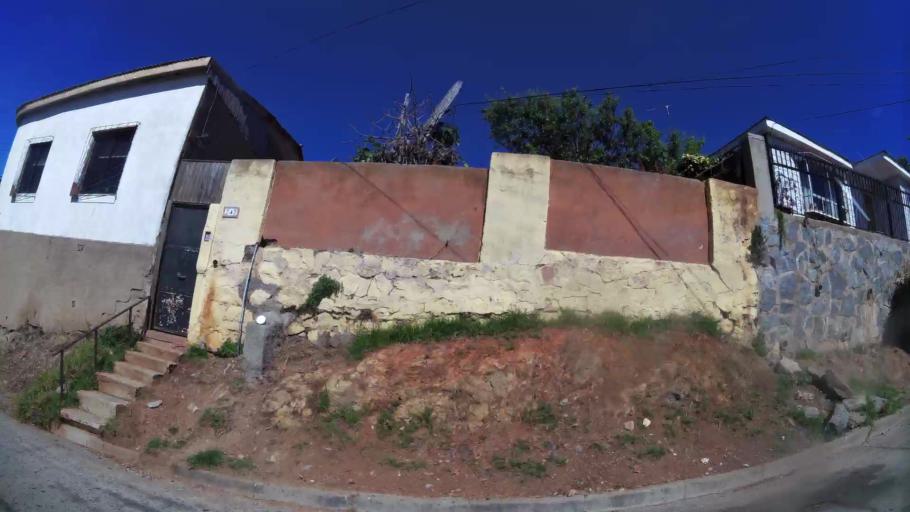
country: CL
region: Valparaiso
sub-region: Provincia de Valparaiso
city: Valparaiso
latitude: -33.0288
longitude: -71.6427
